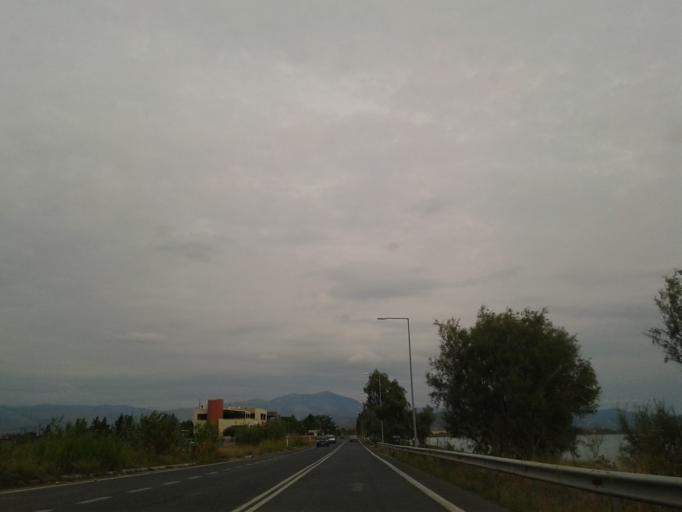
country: GR
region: Peloponnese
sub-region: Nomos Argolidos
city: Nea Kios
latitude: 37.5897
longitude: 22.7628
